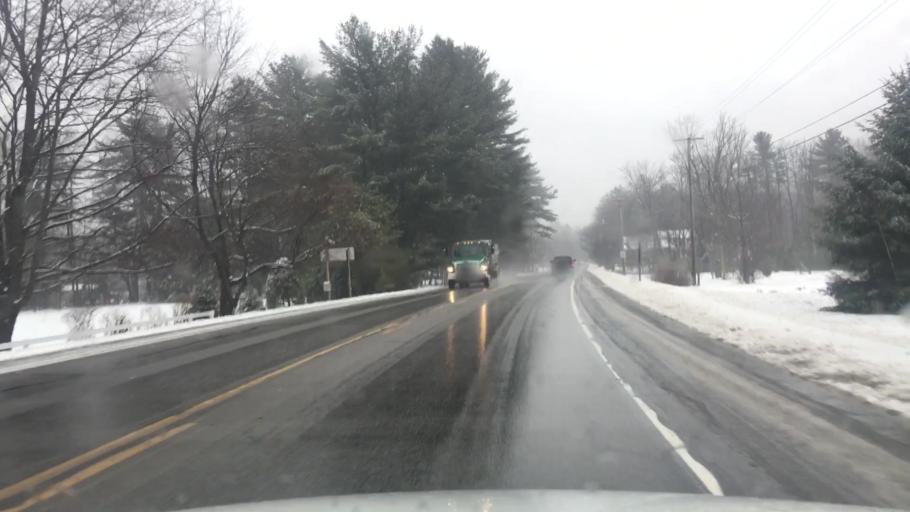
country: US
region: Maine
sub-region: York County
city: Buxton
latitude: 43.6060
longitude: -70.5350
